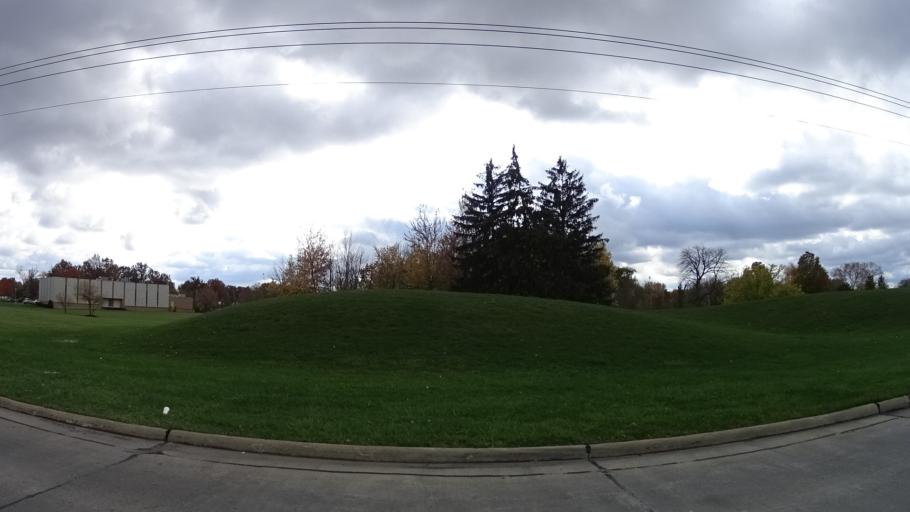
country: US
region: Ohio
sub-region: Lorain County
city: Lorain
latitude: 41.4418
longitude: -82.1957
